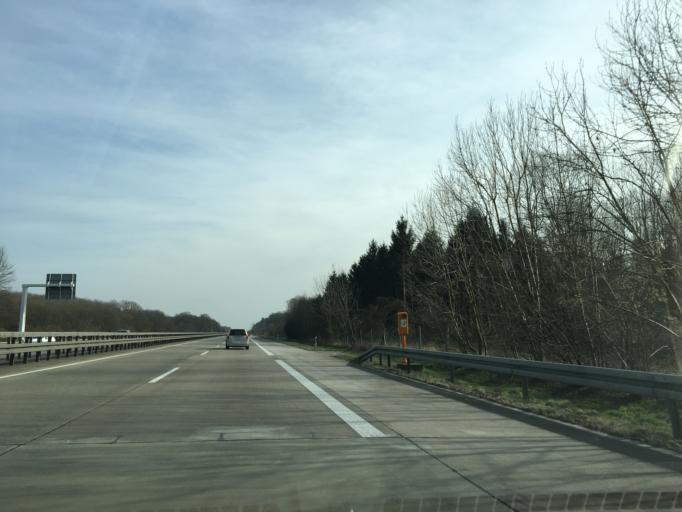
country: DE
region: North Rhine-Westphalia
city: Geseke
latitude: 51.5970
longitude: 8.5295
